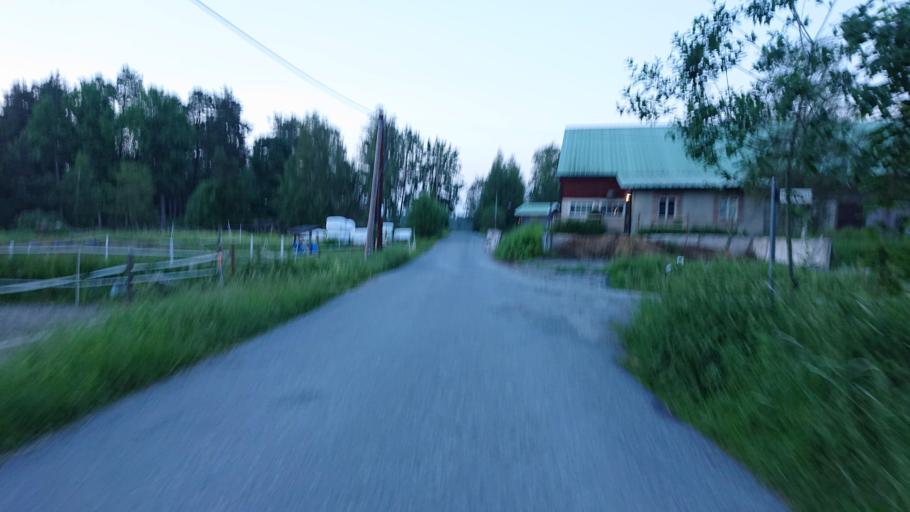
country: SE
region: Stockholm
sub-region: Osterakers Kommun
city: Akersberga
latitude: 59.4739
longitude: 18.2418
